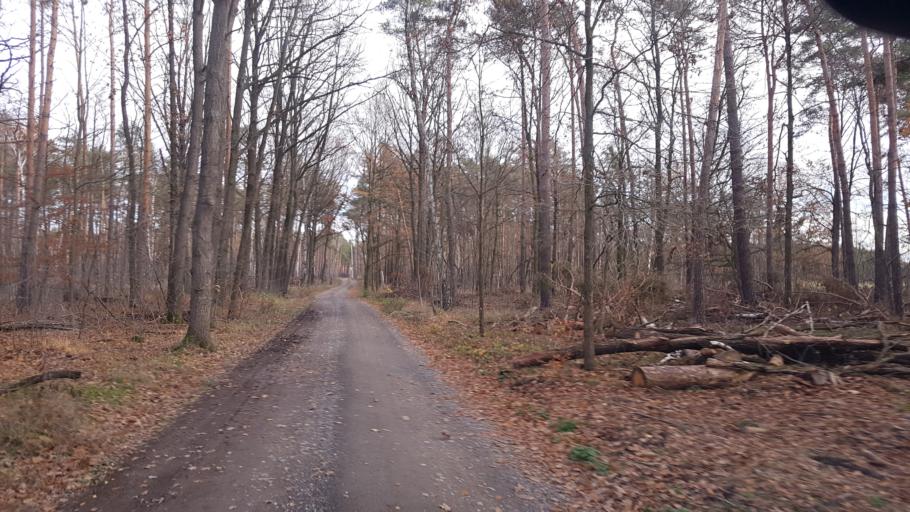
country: DE
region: Brandenburg
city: Falkenberg
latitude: 51.5733
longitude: 13.2706
